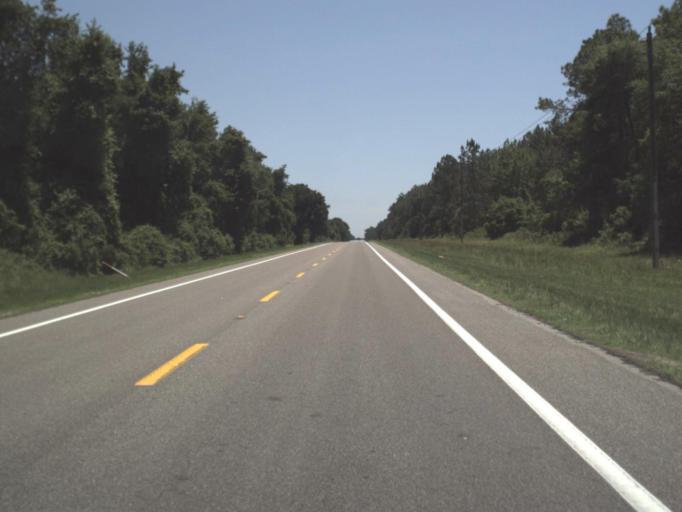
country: US
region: Florida
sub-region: Suwannee County
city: Wellborn
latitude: 30.2408
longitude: -82.8602
